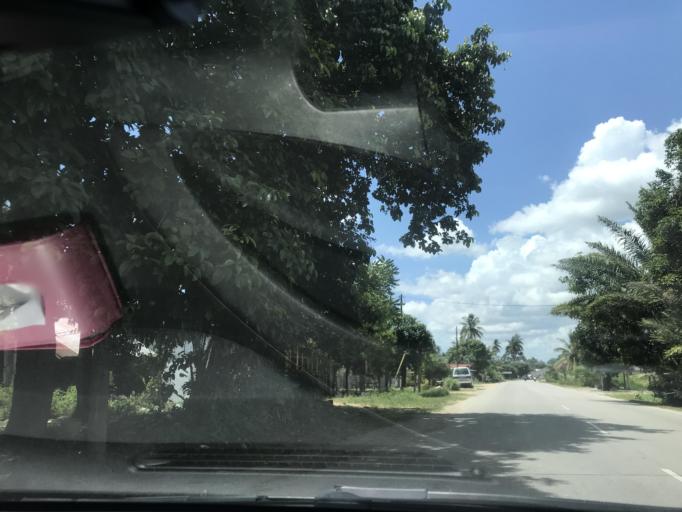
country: MY
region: Kelantan
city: Tumpat
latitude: 6.1994
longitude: 102.1278
